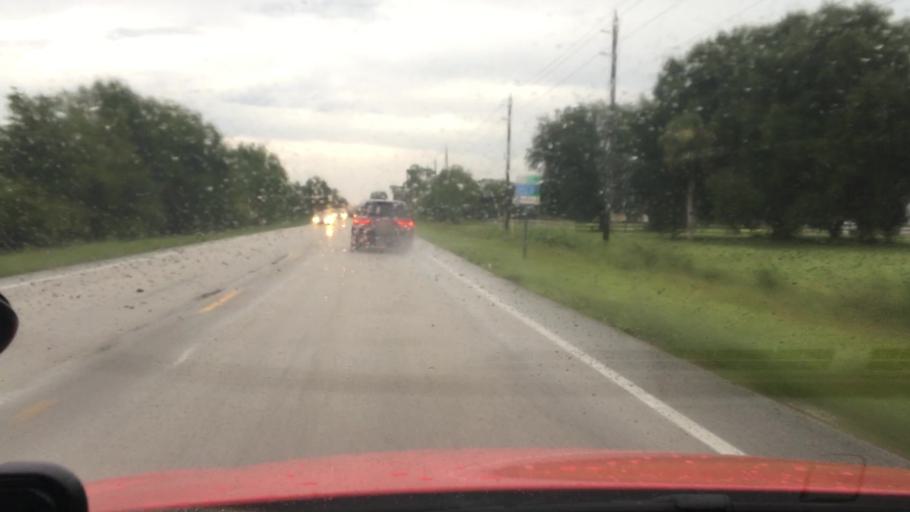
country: US
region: Florida
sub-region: Volusia County
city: Samsula-Spruce Creek
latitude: 29.0682
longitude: -81.0680
